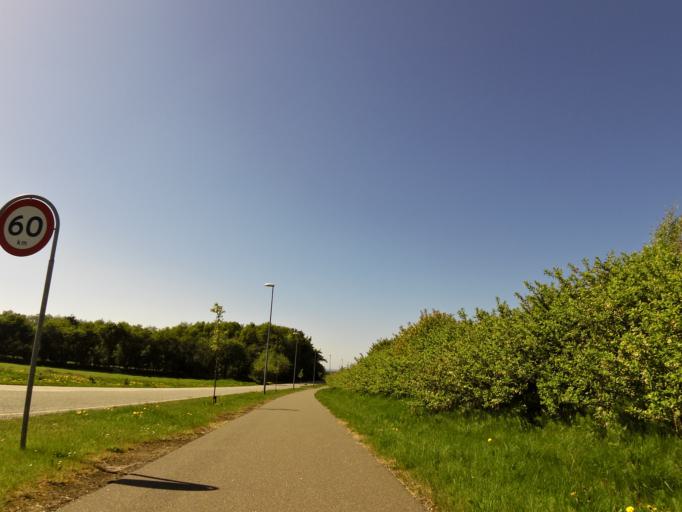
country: DK
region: Central Jutland
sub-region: Holstebro Kommune
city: Vinderup
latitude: 56.4701
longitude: 8.7921
